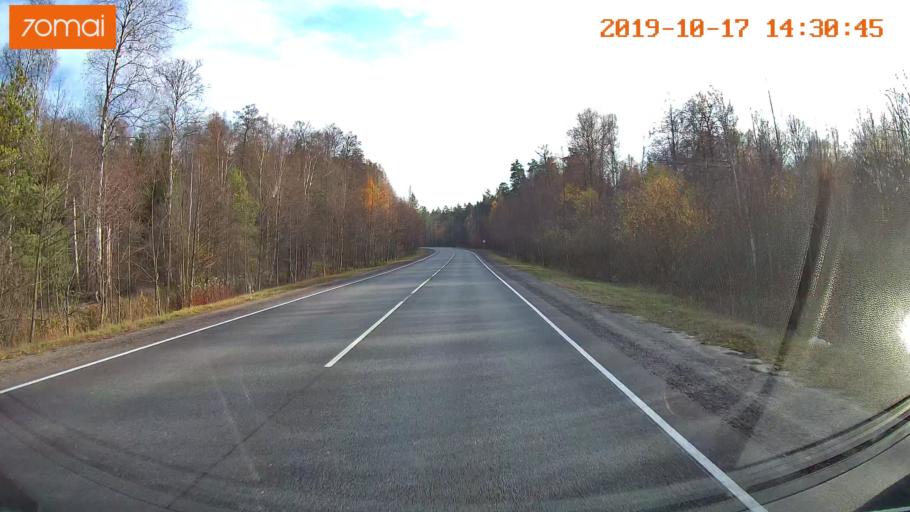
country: RU
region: Rjazan
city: Solotcha
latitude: 54.9435
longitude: 39.9497
